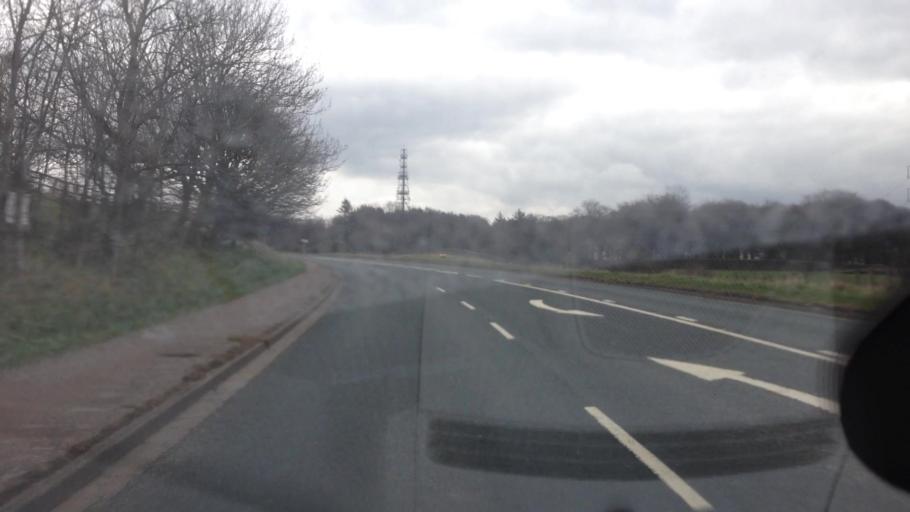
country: GB
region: England
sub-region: Calderdale
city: Elland
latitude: 53.6719
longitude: -1.8207
